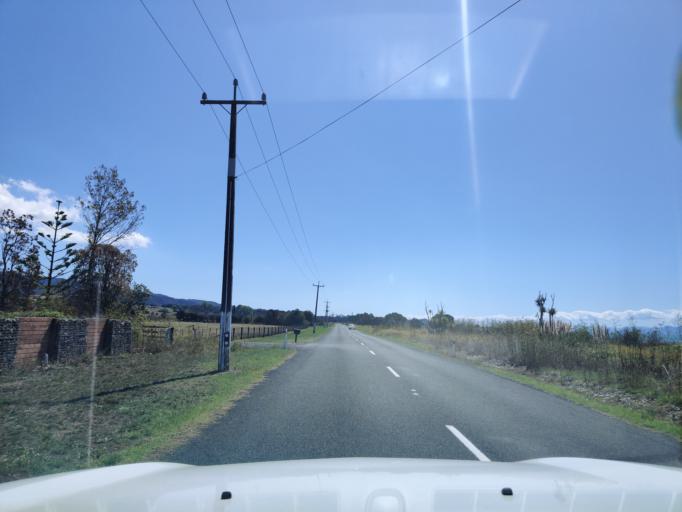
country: NZ
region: Waikato
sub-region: Thames-Coromandel District
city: Thames
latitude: -37.0750
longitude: 175.2960
